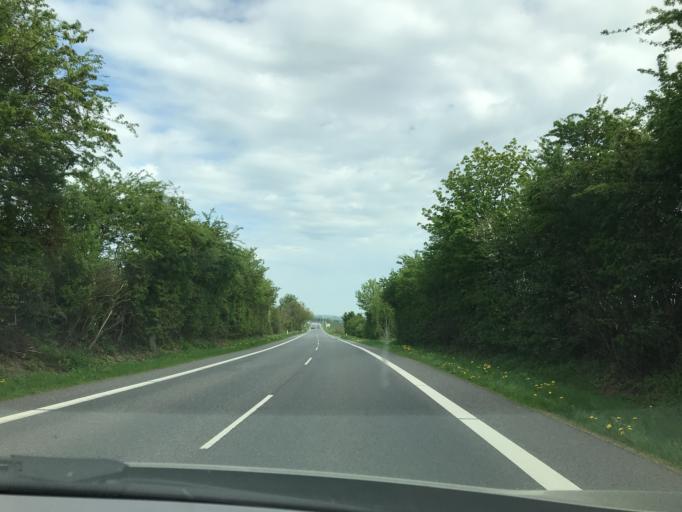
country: DK
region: South Denmark
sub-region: Assens Kommune
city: Assens
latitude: 55.2915
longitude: 9.9328
